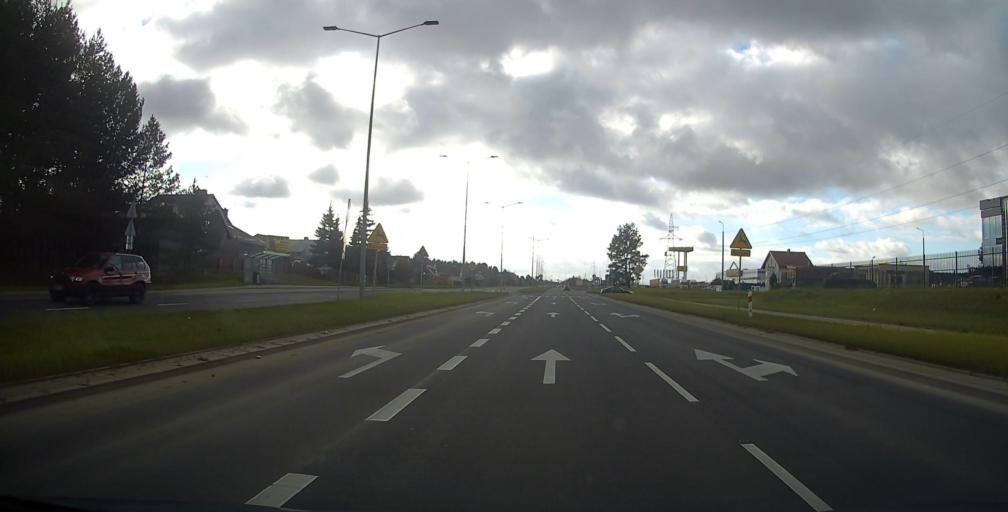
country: PL
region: Warmian-Masurian Voivodeship
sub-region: Powiat elcki
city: Elk
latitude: 53.8153
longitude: 22.3848
